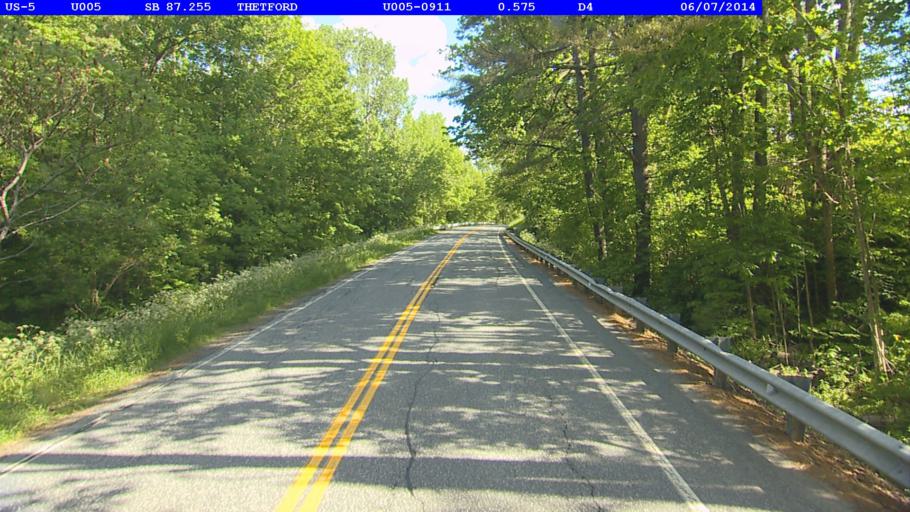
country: US
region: New Hampshire
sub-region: Grafton County
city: Lyme
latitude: 43.7800
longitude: -72.2061
